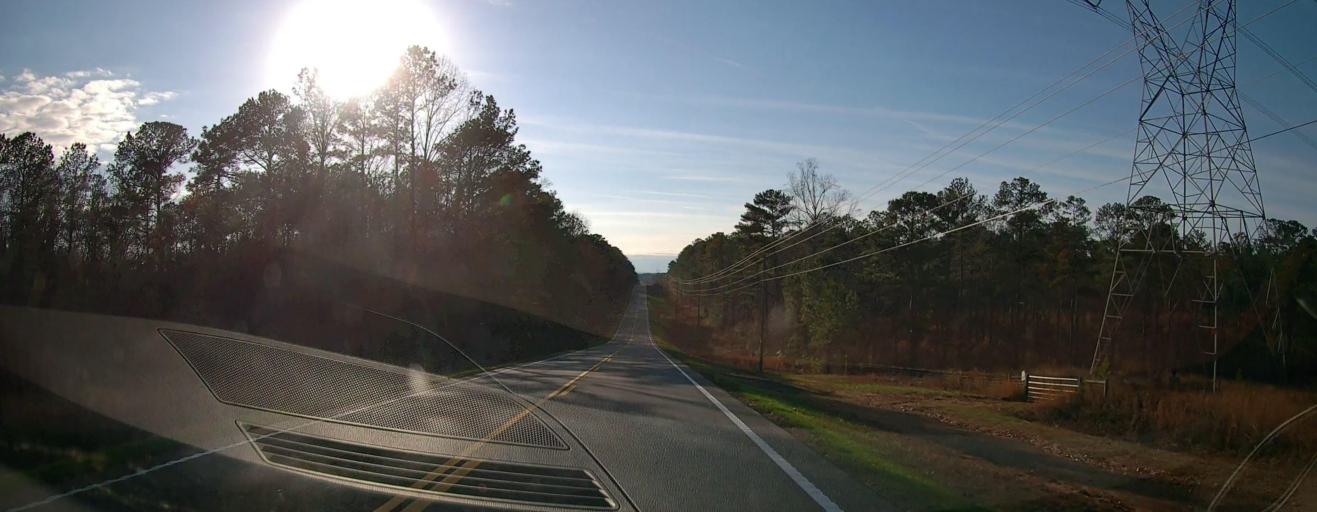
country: US
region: Georgia
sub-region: Harris County
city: Hamilton
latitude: 32.7471
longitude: -84.9853
